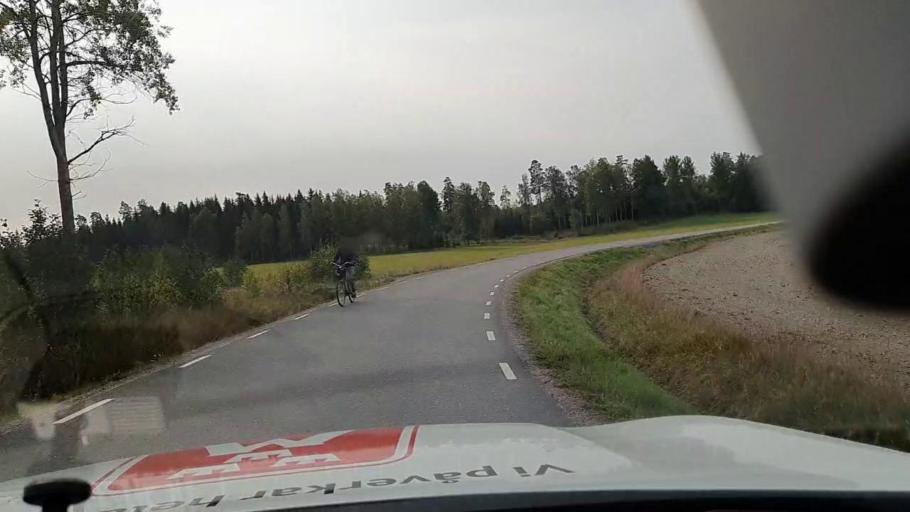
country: SE
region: Soedermanland
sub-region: Nykopings Kommun
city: Nykoping
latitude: 58.8543
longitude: 16.9575
